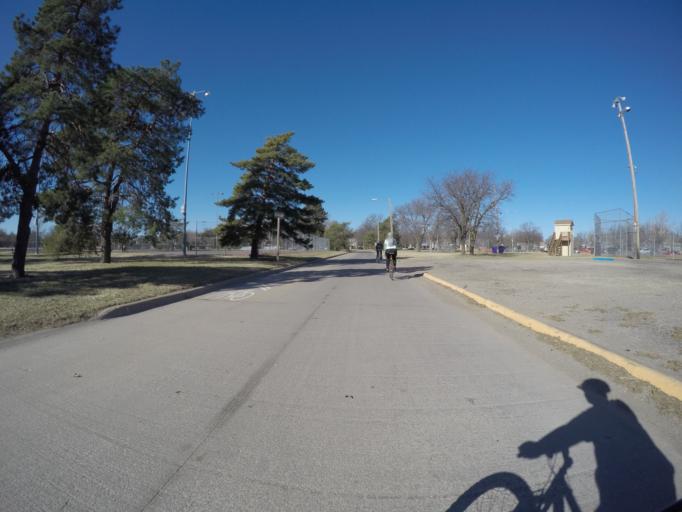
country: US
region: Kansas
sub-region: Riley County
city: Manhattan
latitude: 39.1821
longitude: -96.5755
